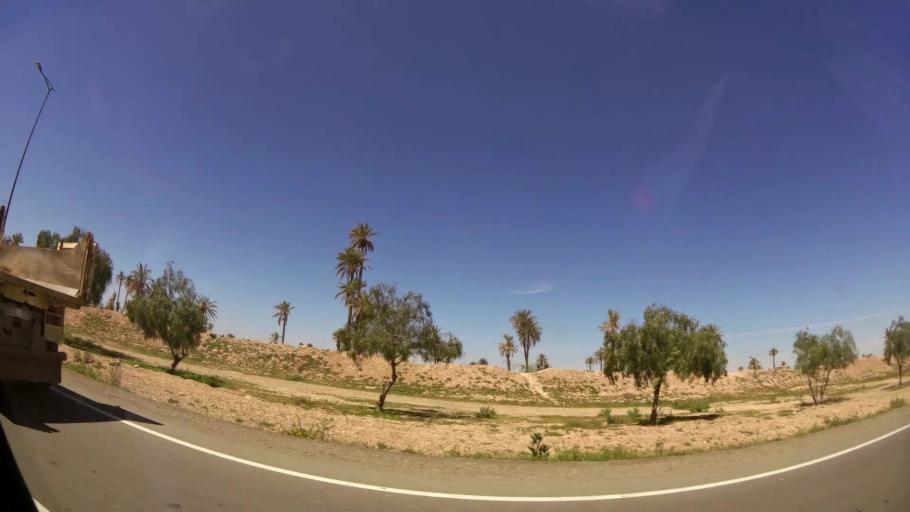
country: MA
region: Marrakech-Tensift-Al Haouz
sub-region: Marrakech
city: Marrakesh
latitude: 31.6691
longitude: -7.9905
